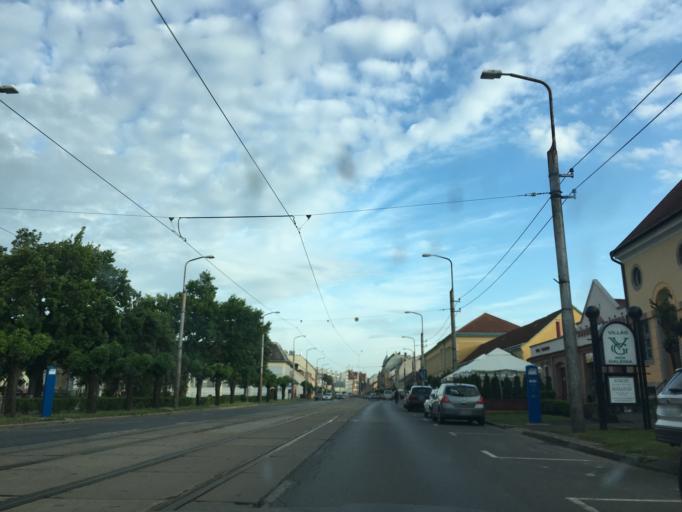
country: HU
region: Hajdu-Bihar
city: Debrecen
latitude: 47.5399
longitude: 21.6252
